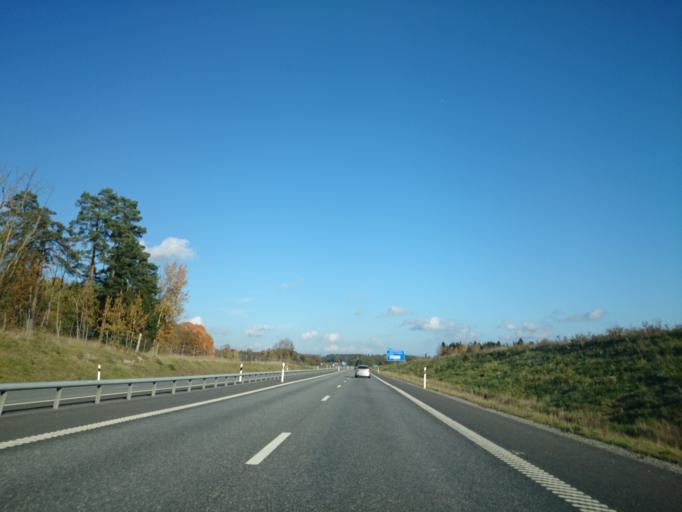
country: SE
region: Stockholm
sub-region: Haninge Kommun
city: Jordbro
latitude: 59.0958
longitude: 18.1059
